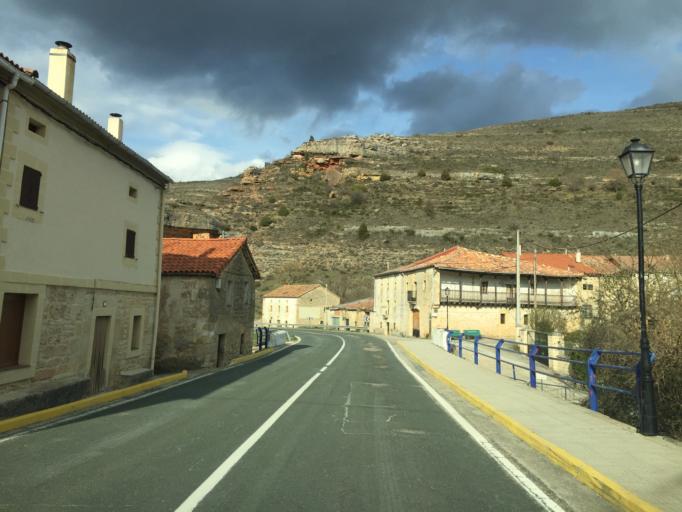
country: ES
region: Castille and Leon
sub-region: Provincia de Burgos
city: Tubilla del Agua
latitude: 42.7090
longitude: -3.8026
